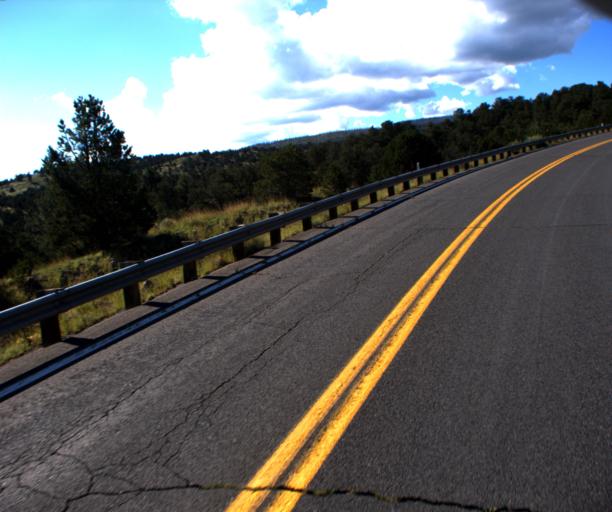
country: US
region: Arizona
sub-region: Apache County
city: Eagar
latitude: 34.0913
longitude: -109.3417
